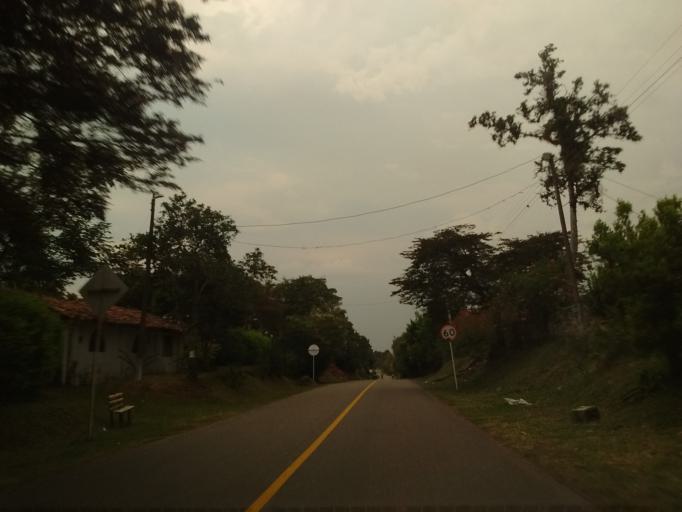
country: CO
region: Cauca
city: Caloto
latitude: 3.0747
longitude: -76.3512
